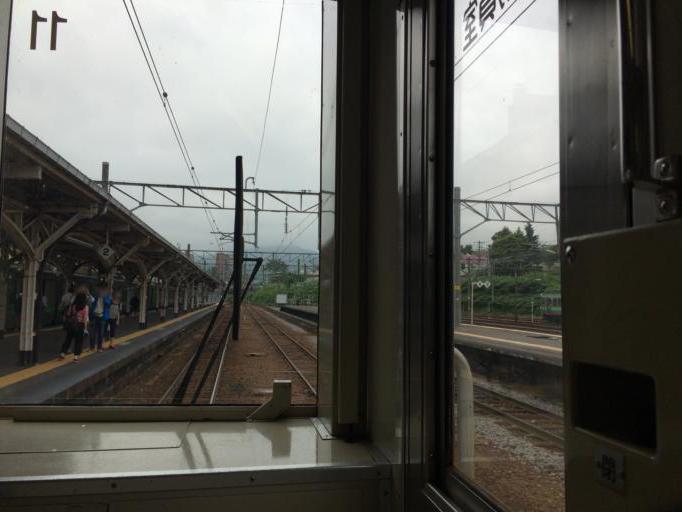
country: JP
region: Hokkaido
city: Otaru
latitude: 43.1971
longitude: 140.9937
